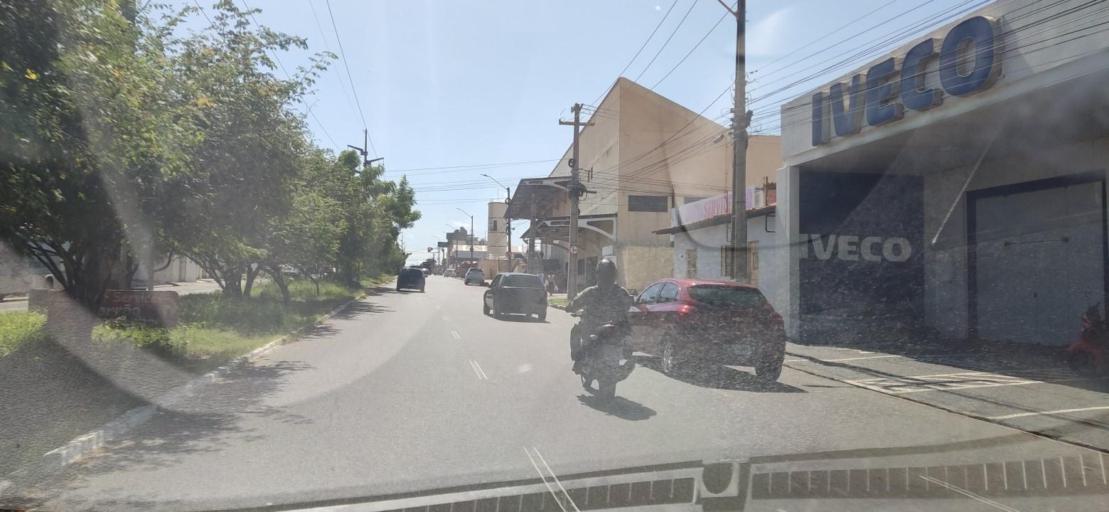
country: BR
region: Piaui
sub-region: Teresina
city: Teresina
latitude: -5.1205
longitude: -42.8048
